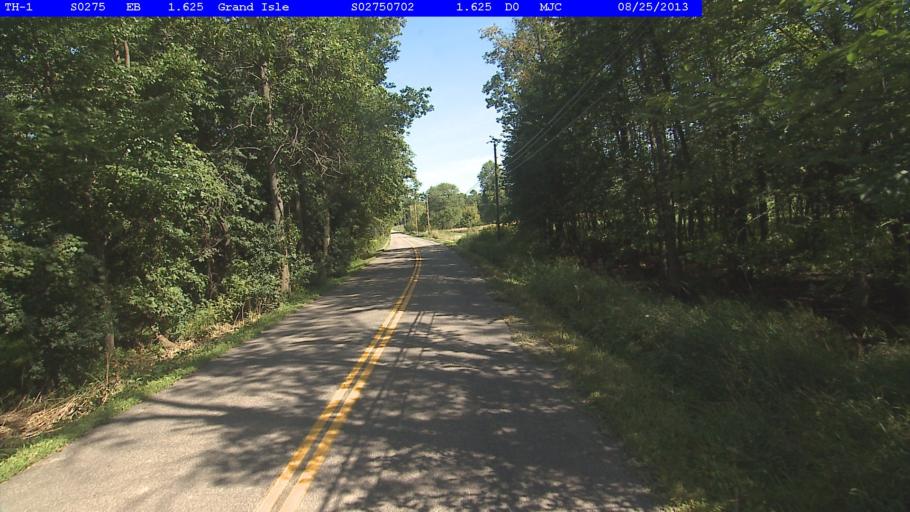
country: US
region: New York
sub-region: Clinton County
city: Cumberland Head
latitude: 44.7233
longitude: -73.3386
